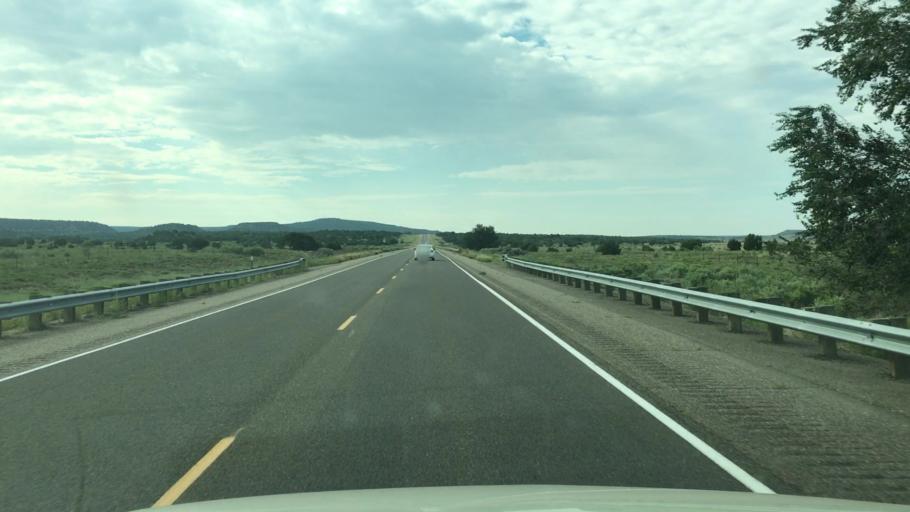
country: US
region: New Mexico
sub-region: Santa Fe County
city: Eldorado at Santa Fe
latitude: 35.3431
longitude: -105.8416
